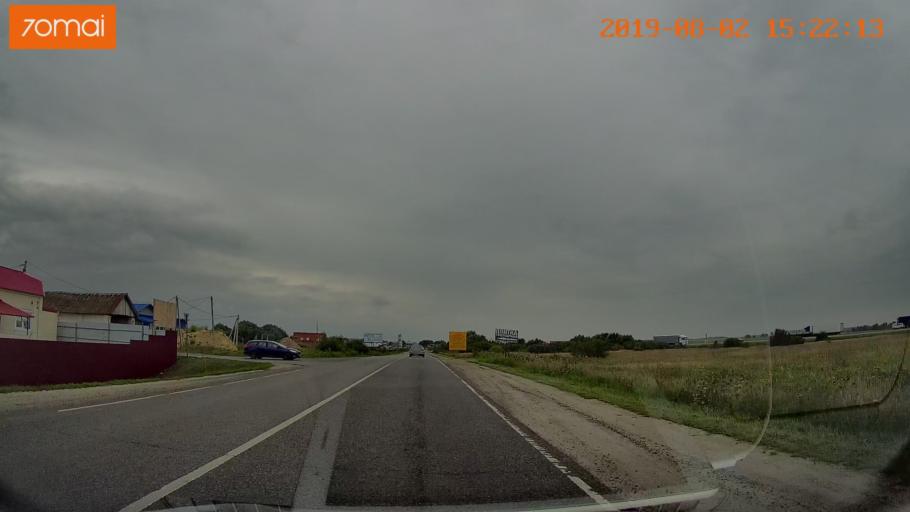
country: RU
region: Moskovskaya
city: Voskresensk
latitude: 55.3106
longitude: 38.6167
